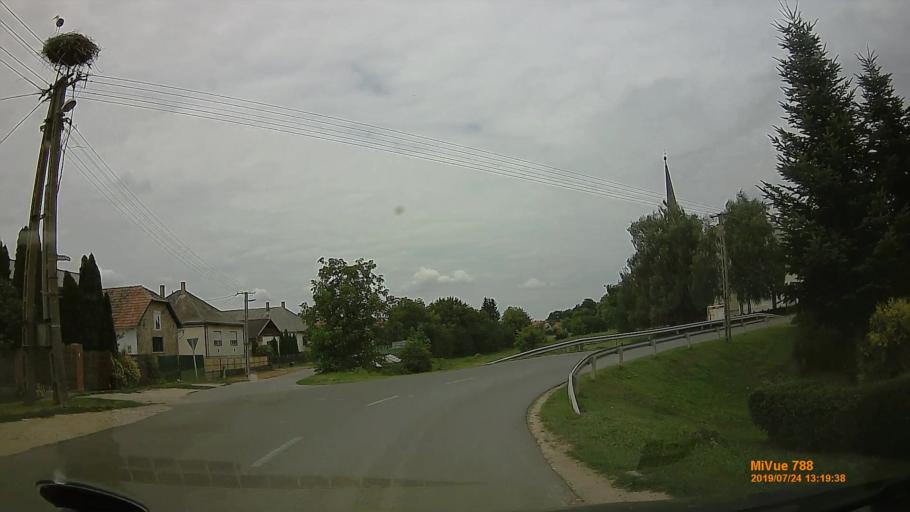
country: HU
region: Szabolcs-Szatmar-Bereg
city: Vasarosnameny
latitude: 48.1987
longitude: 22.4074
